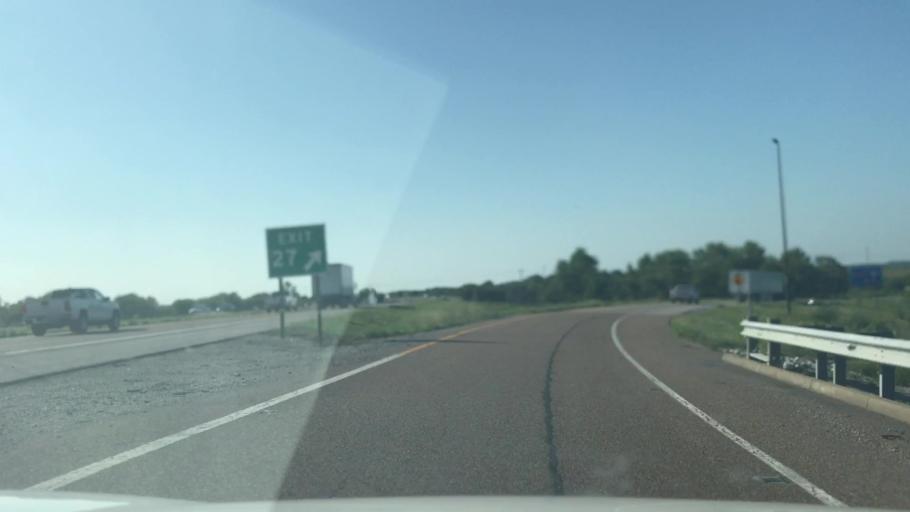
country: US
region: Illinois
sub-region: Clinton County
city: New Baden
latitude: 38.5327
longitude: -89.7264
